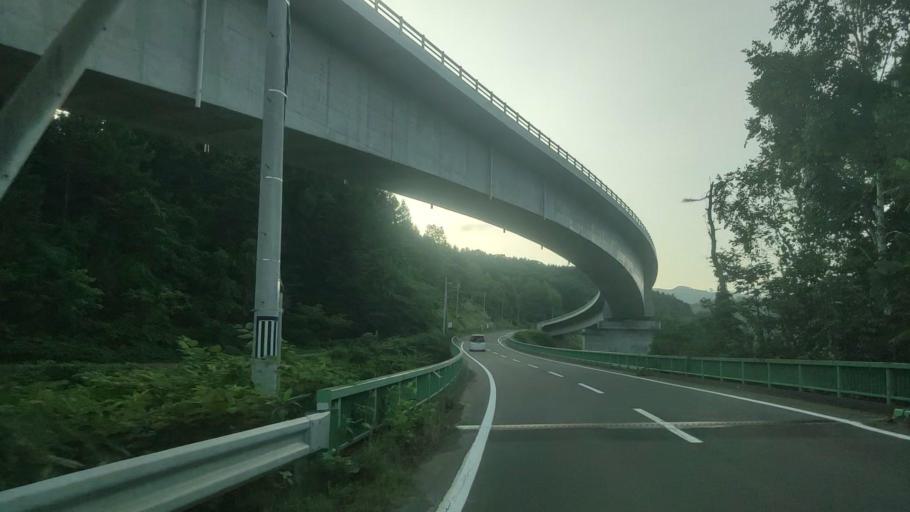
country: JP
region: Hokkaido
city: Bibai
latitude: 43.2271
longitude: 142.0437
